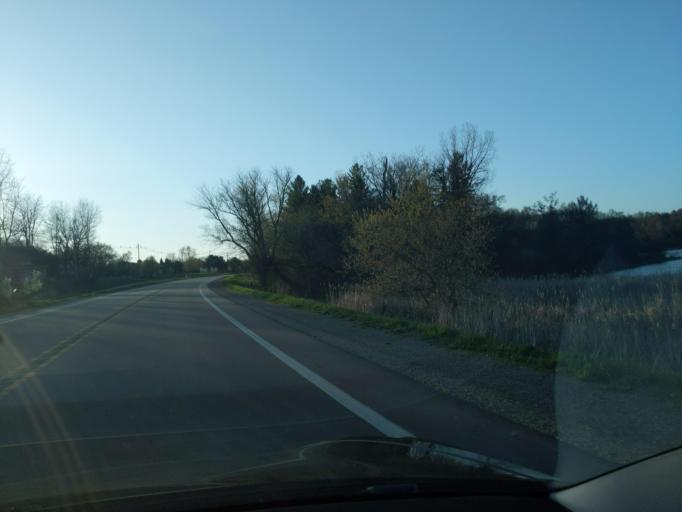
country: US
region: Michigan
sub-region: Washtenaw County
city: Chelsea
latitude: 42.3511
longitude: -84.0522
